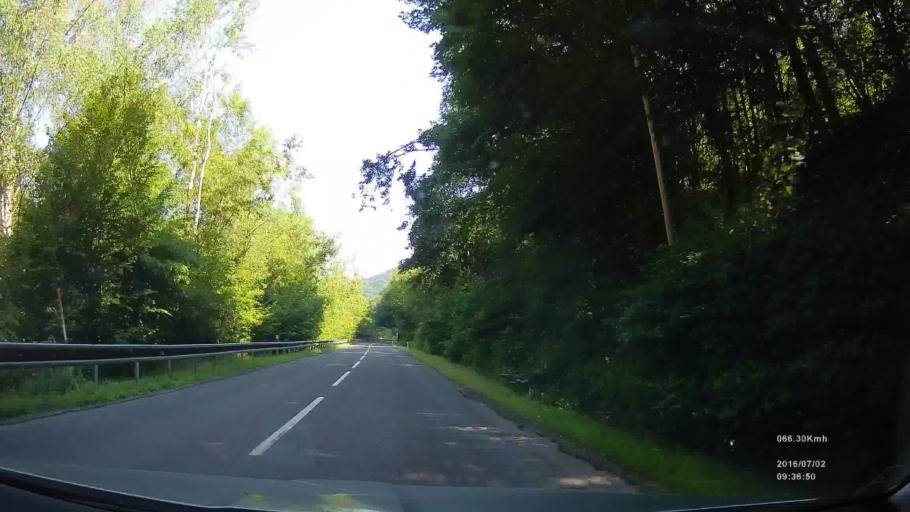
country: SK
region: Kosicky
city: Gelnica
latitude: 48.8214
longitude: 21.0811
